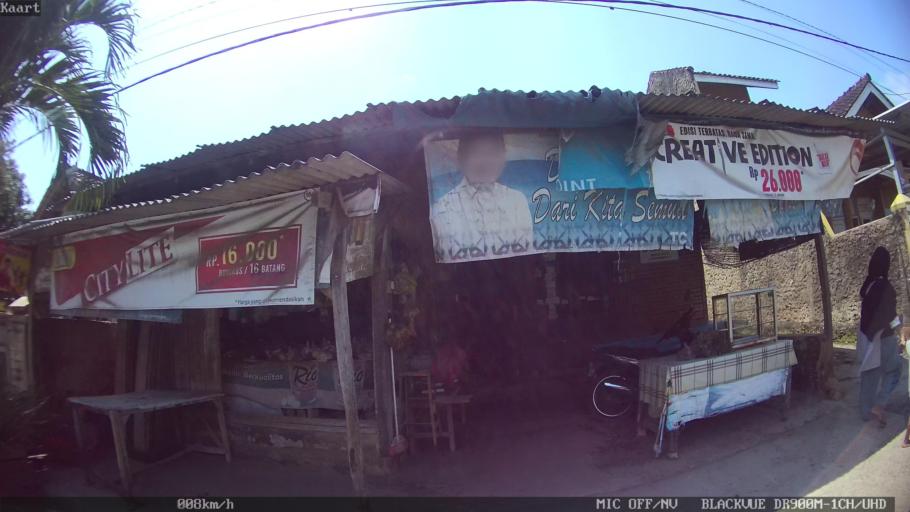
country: ID
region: Lampung
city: Kedaton
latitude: -5.3576
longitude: 105.2772
